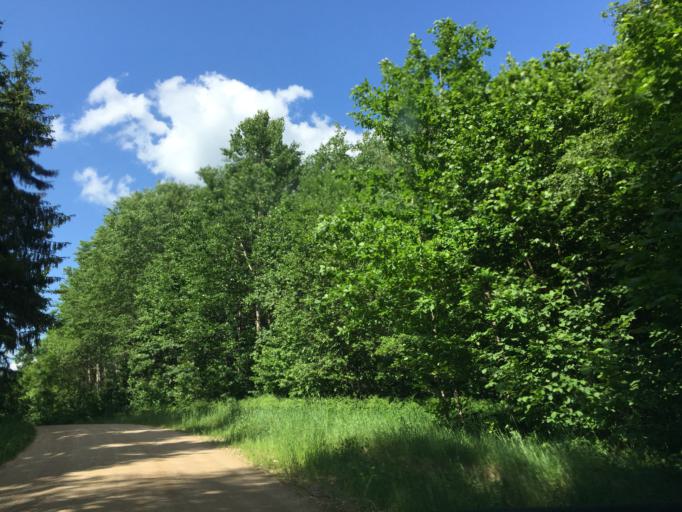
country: LV
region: Priekuli
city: Priekuli
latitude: 57.2493
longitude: 25.4053
